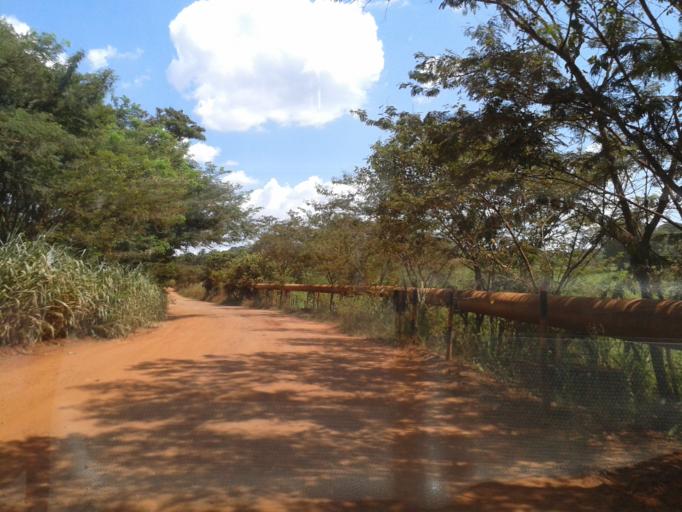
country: BR
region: Minas Gerais
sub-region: Ituiutaba
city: Ituiutaba
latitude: -19.0361
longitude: -49.6981
